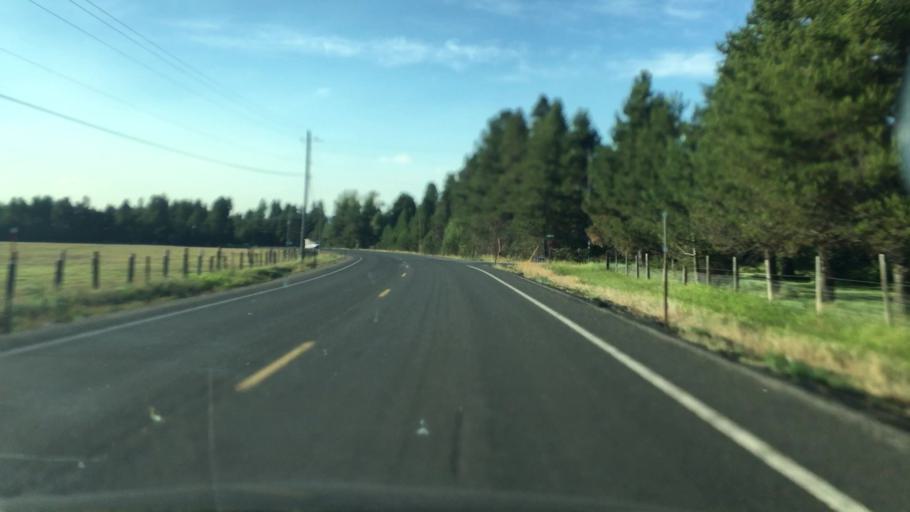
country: US
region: Idaho
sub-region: Valley County
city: McCall
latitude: 44.8222
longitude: -116.0781
